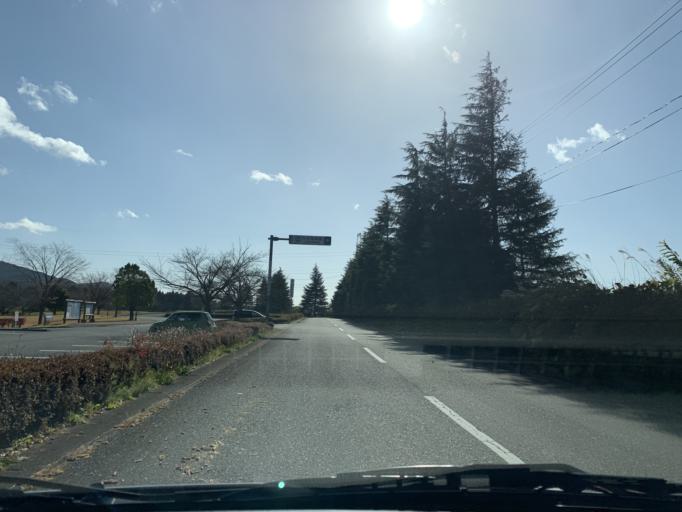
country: JP
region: Iwate
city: Mizusawa
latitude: 39.0269
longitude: 141.1231
